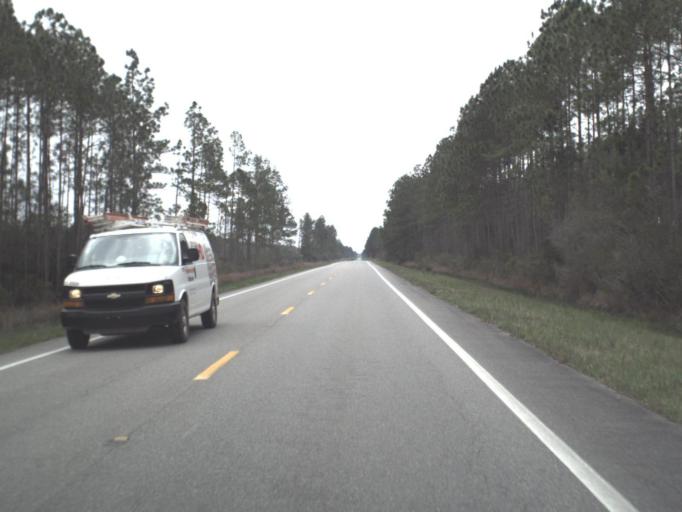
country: US
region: Florida
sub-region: Gulf County
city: Port Saint Joe
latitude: 29.9260
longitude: -85.1960
